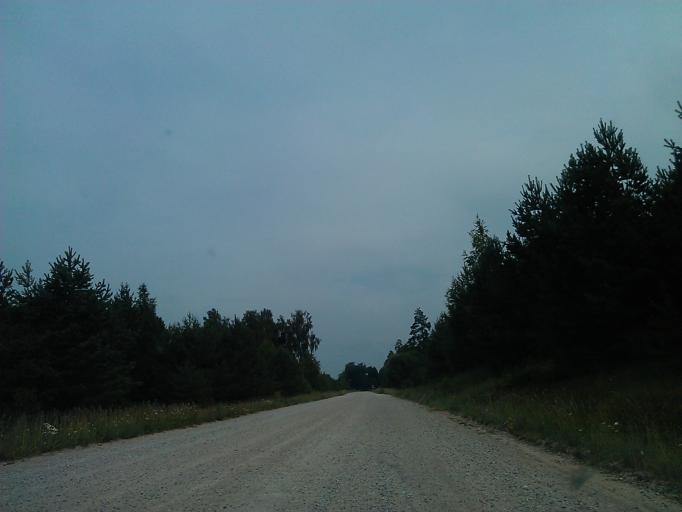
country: LV
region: Burtnieki
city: Matisi
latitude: 57.6354
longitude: 25.2469
